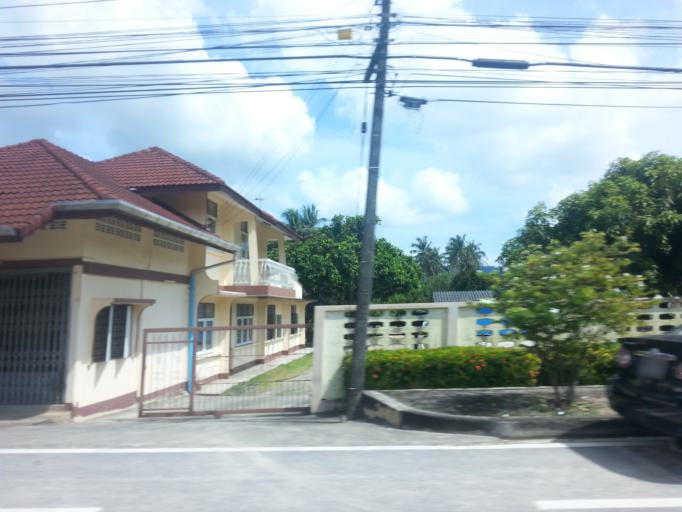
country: TH
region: Phuket
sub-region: Amphoe Kathu
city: Kathu
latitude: 7.9148
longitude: 98.3323
